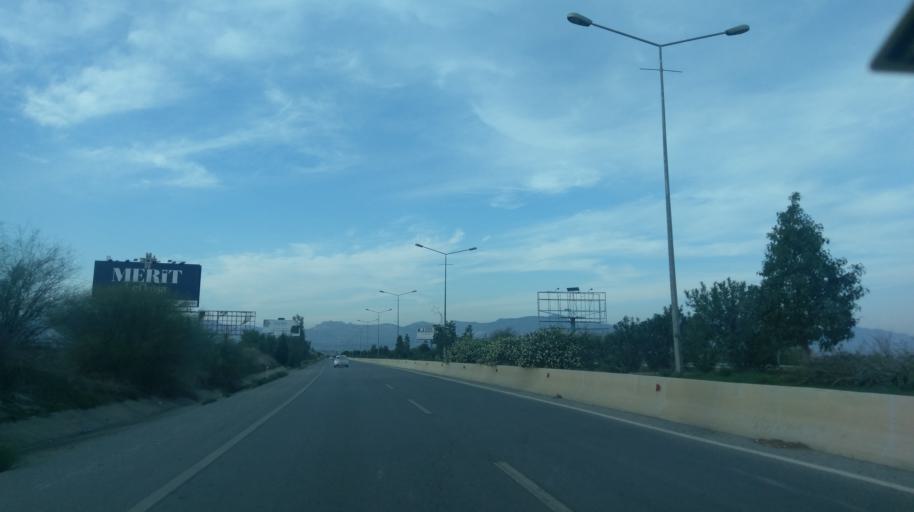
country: CY
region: Lefkosia
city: Geri
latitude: 35.1705
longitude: 33.5033
